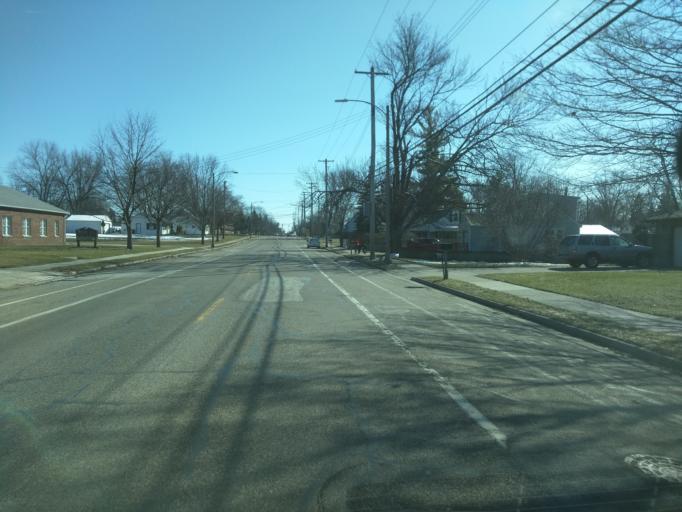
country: US
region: Michigan
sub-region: Ingham County
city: Lansing
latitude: 42.7004
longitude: -84.5822
